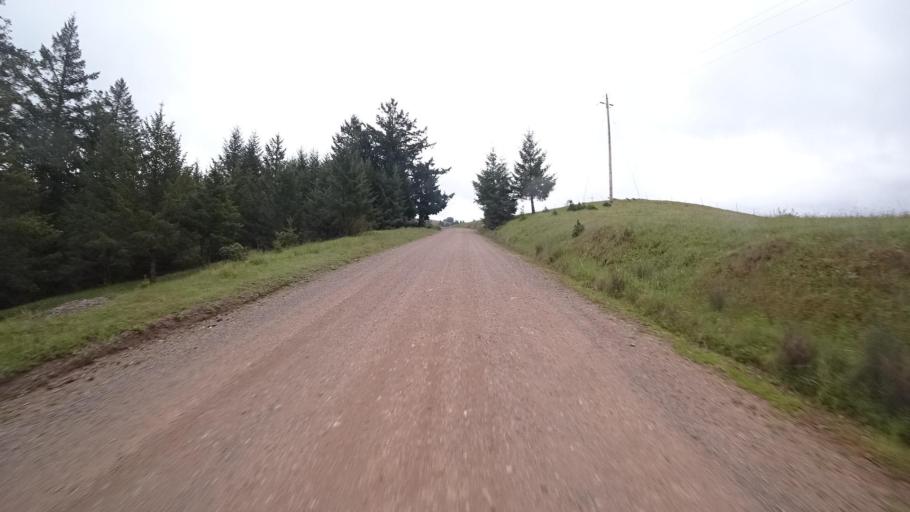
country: US
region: California
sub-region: Humboldt County
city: Redway
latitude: 40.2194
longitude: -123.7554
